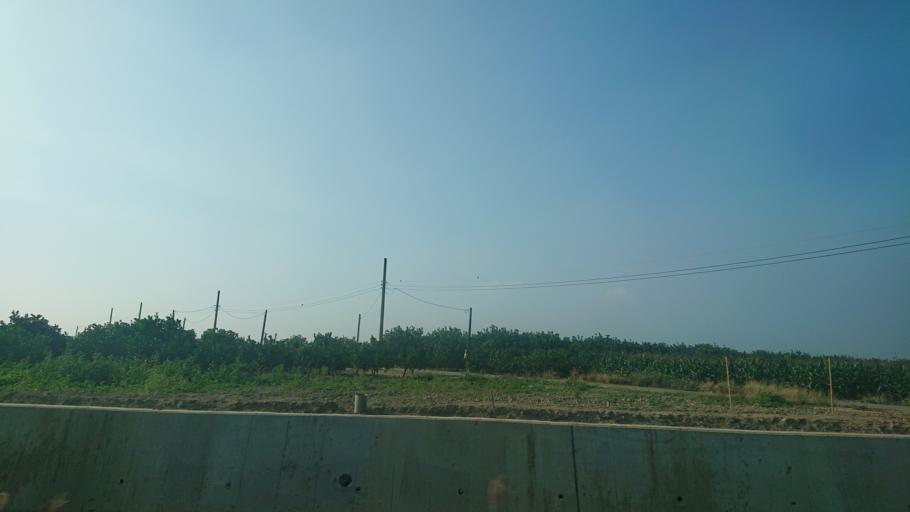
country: TW
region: Taiwan
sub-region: Tainan
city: Tainan
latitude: 23.1397
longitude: 120.2426
